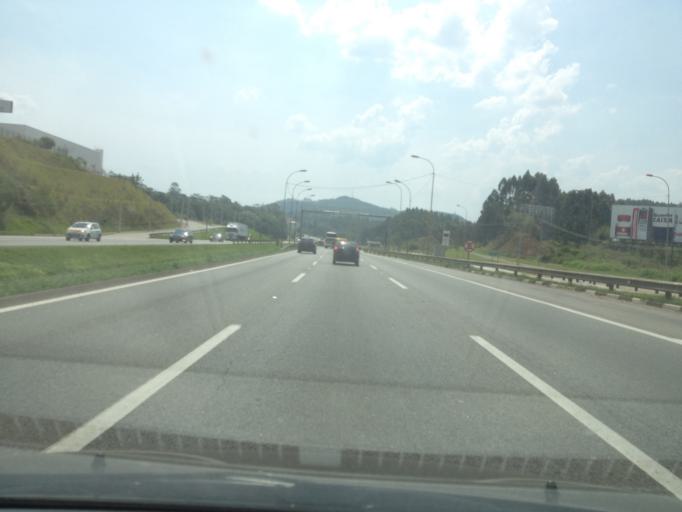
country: BR
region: Sao Paulo
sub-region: Pirapora Do Bom Jesus
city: Pirapora do Bom Jesus
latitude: -23.4780
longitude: -46.9985
